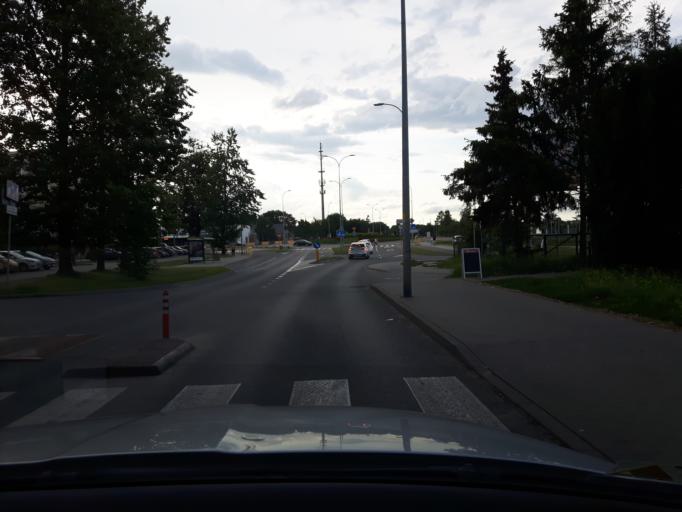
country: PL
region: Pomeranian Voivodeship
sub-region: Sopot
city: Sopot
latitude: 54.4240
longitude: 18.5782
